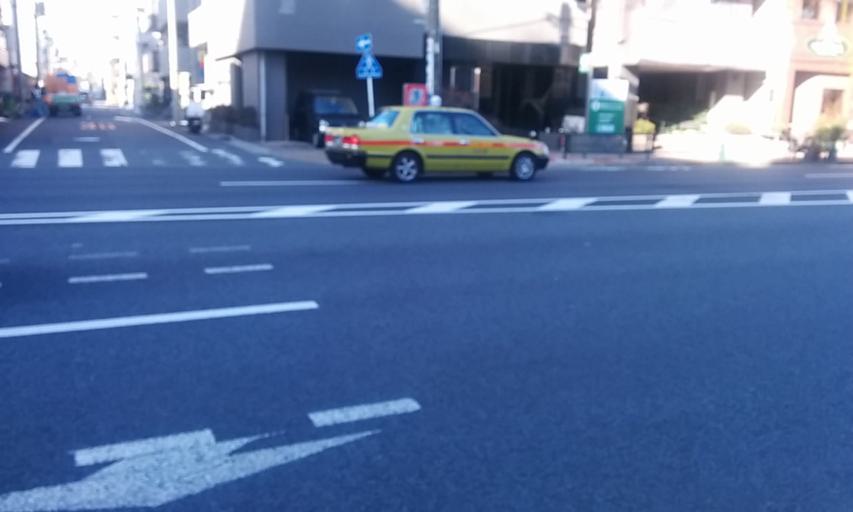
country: JP
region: Tokyo
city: Urayasu
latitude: 35.7094
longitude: 139.8043
